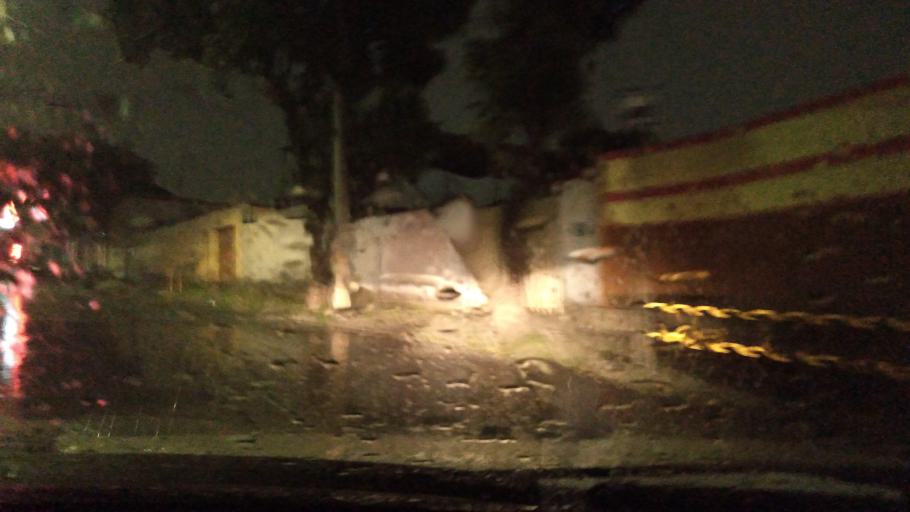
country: BR
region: Minas Gerais
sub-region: Belo Horizonte
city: Belo Horizonte
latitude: -19.8778
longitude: -43.9389
